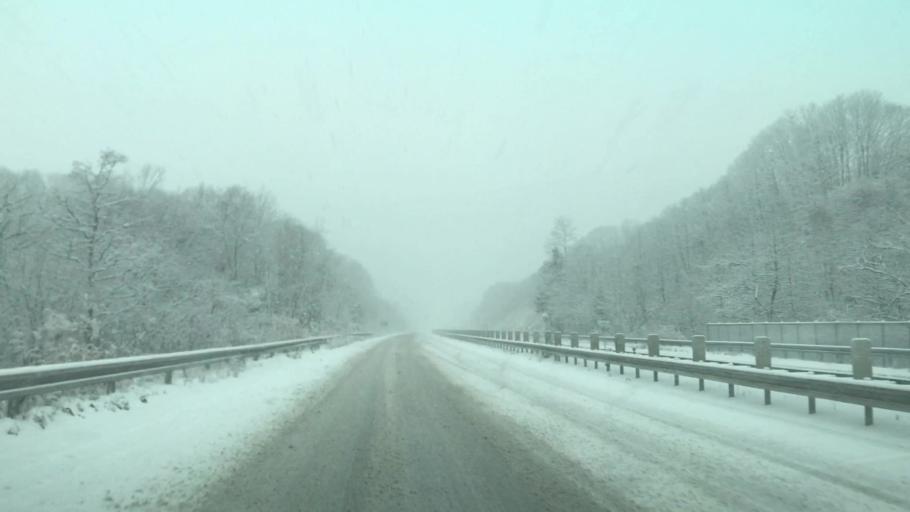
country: JP
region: Hokkaido
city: Muroran
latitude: 42.4347
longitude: 141.1238
